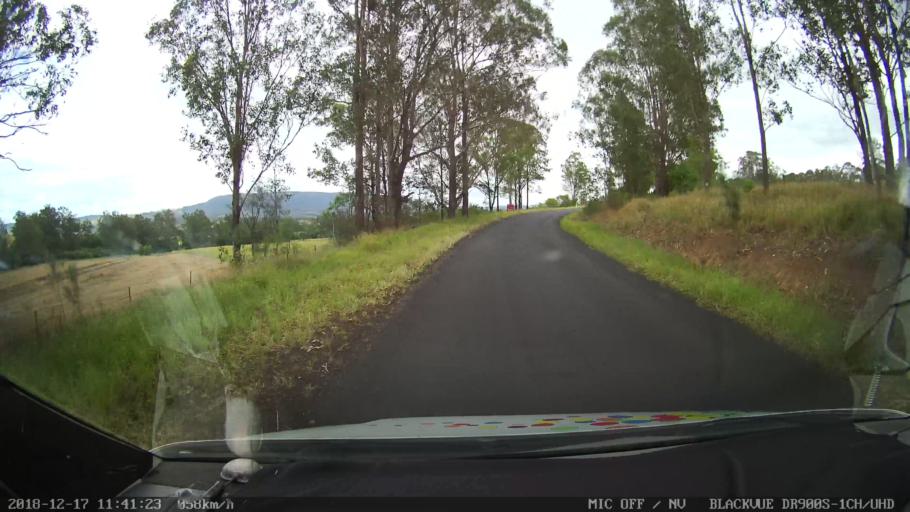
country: AU
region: New South Wales
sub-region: Kyogle
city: Kyogle
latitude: -28.6752
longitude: 152.5887
